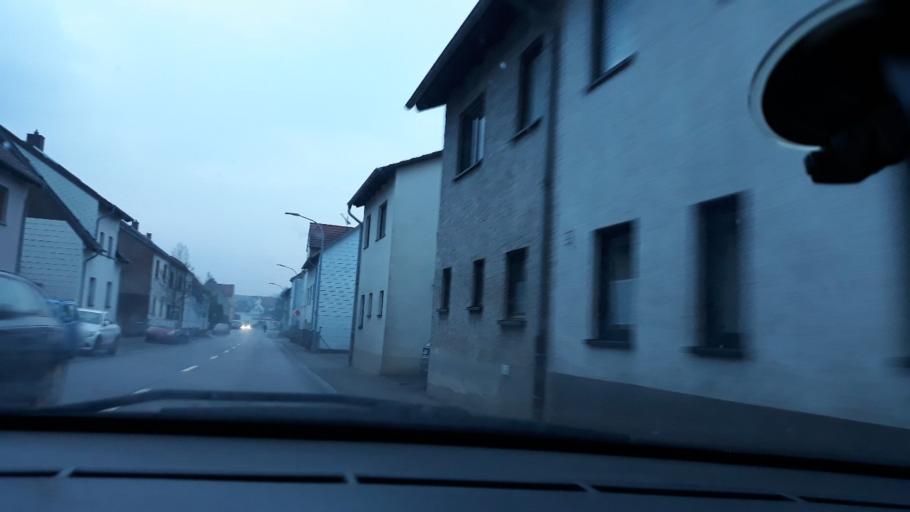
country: DE
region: Saarland
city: Kirkel
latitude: 49.2446
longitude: 7.2089
